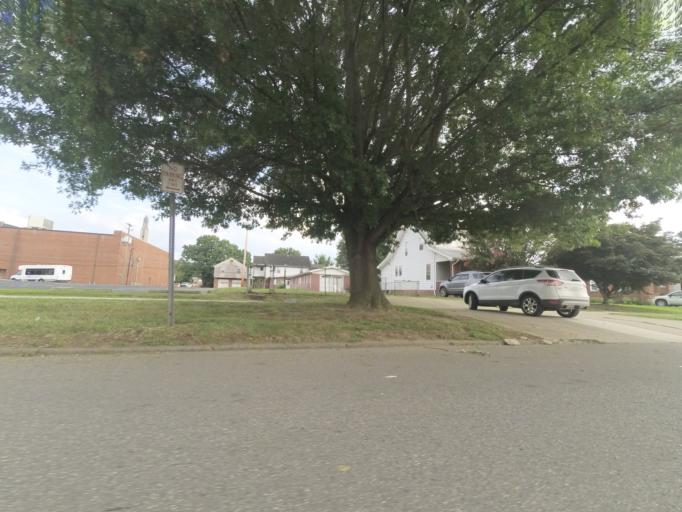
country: US
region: West Virginia
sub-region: Cabell County
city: Huntington
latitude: 38.4315
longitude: -82.4044
